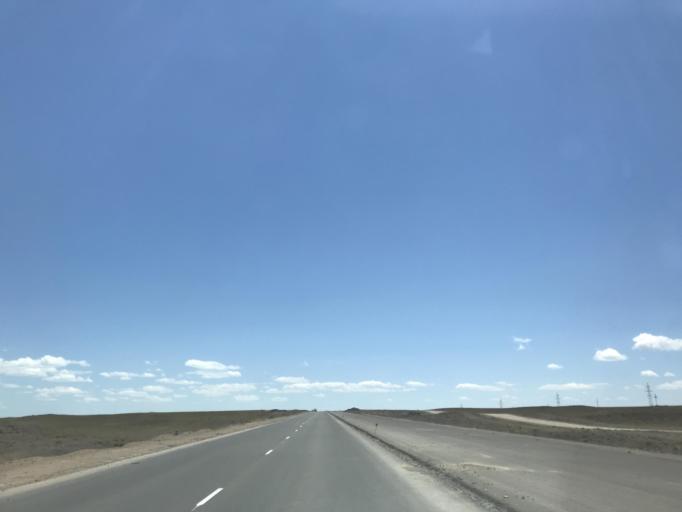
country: KZ
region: Zhambyl
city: Mynaral
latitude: 45.2707
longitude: 73.7894
